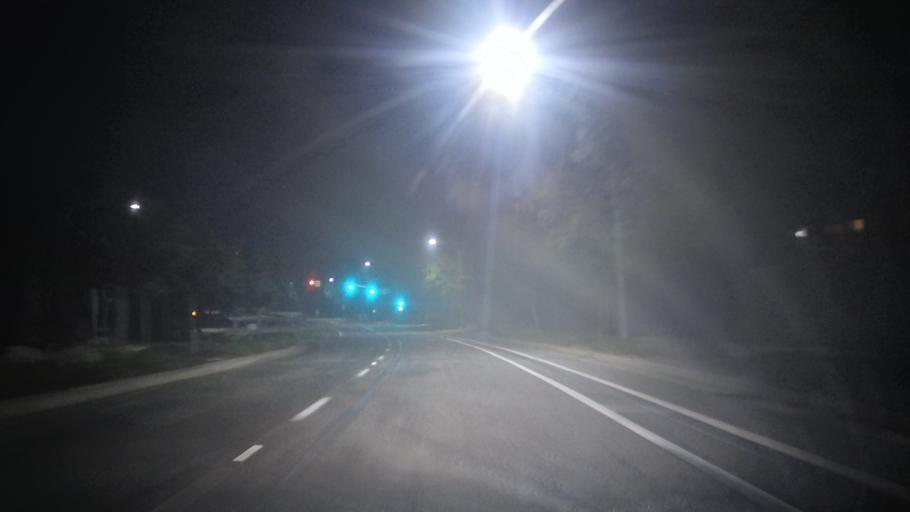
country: US
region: California
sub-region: San Diego County
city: Fairbanks Ranch
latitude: 33.0097
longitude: -117.1169
